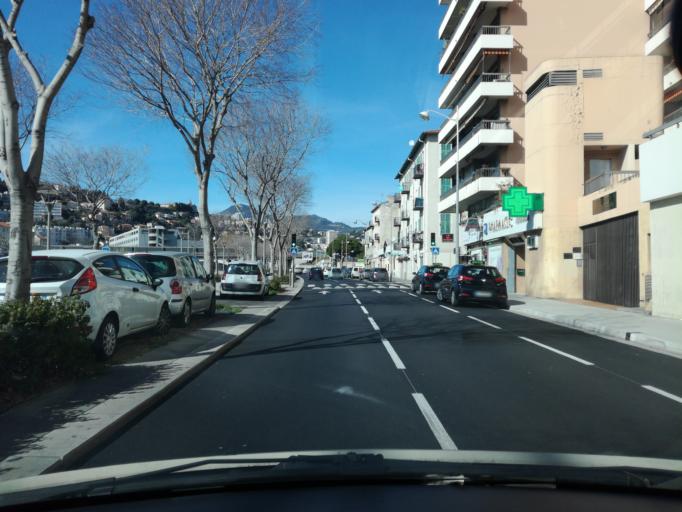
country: FR
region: Provence-Alpes-Cote d'Azur
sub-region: Departement des Alpes-Maritimes
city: Nice
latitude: 43.7126
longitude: 7.2841
